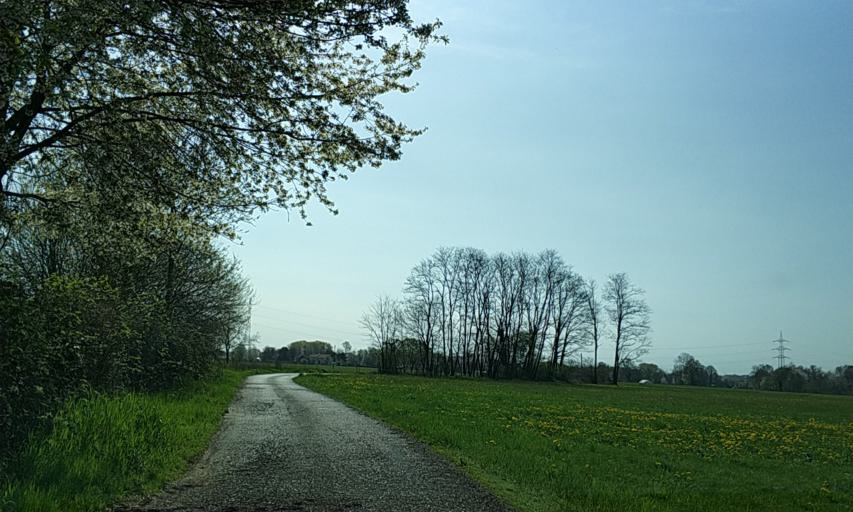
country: IT
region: Piedmont
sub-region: Provincia di Torino
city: Cafasse
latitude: 45.2358
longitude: 7.5338
